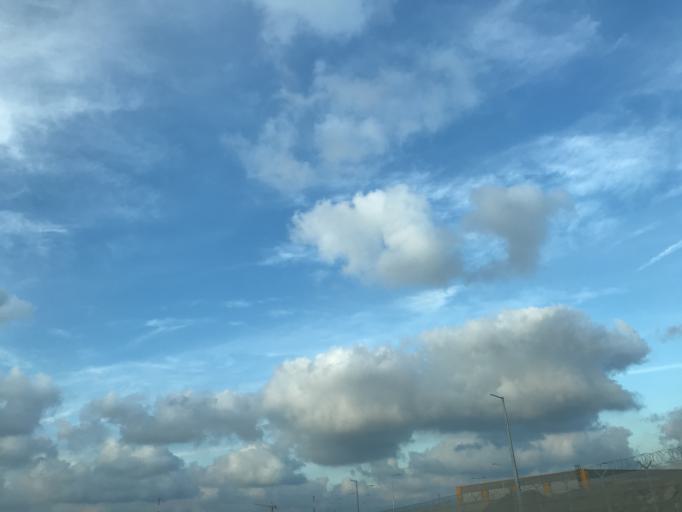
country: TR
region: Istanbul
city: Durusu
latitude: 41.2624
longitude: 28.7144
